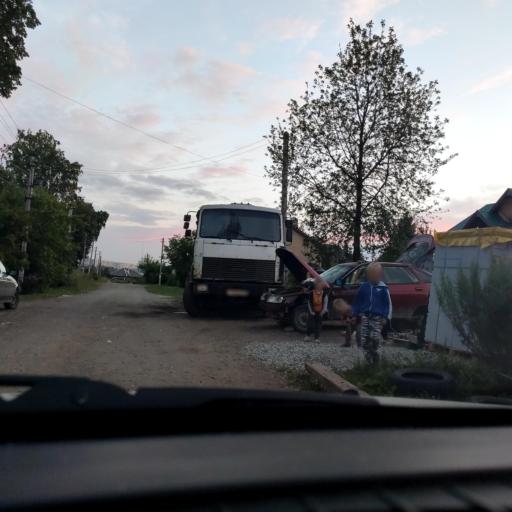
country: RU
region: Perm
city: Perm
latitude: 58.0456
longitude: 56.3324
